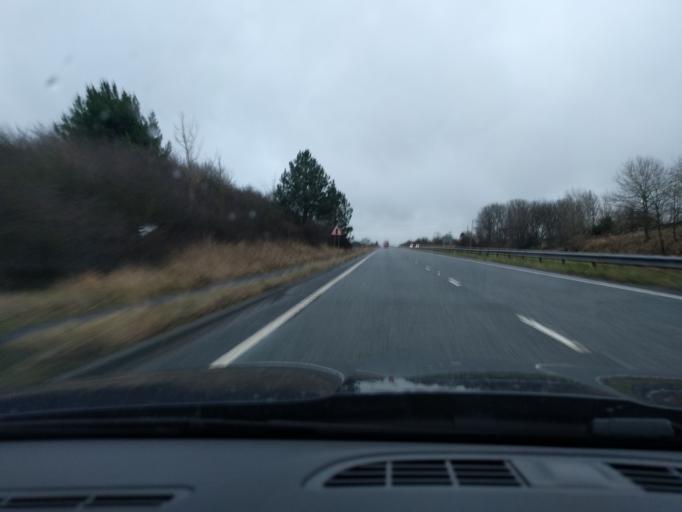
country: GB
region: England
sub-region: Northumberland
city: Berwick-Upon-Tweed
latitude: 55.8000
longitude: -2.0365
